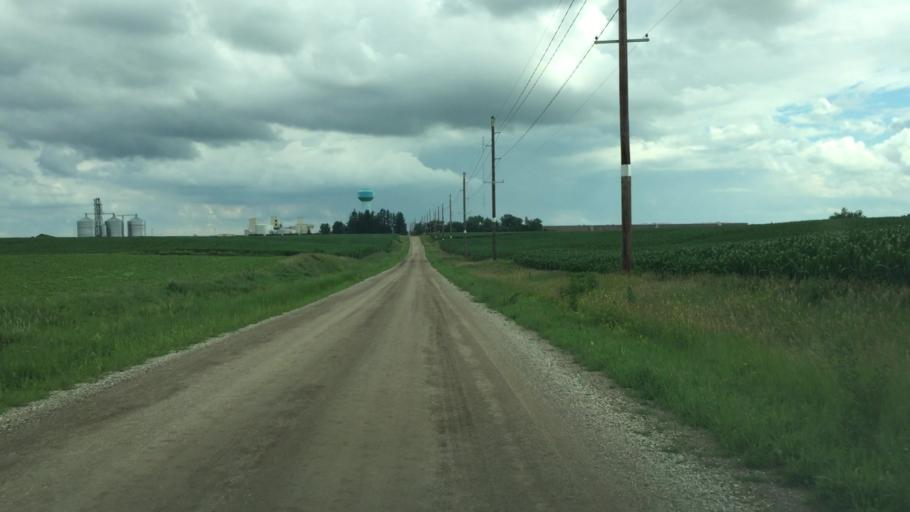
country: US
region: Iowa
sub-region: Jasper County
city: Newton
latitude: 41.7437
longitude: -93.0195
